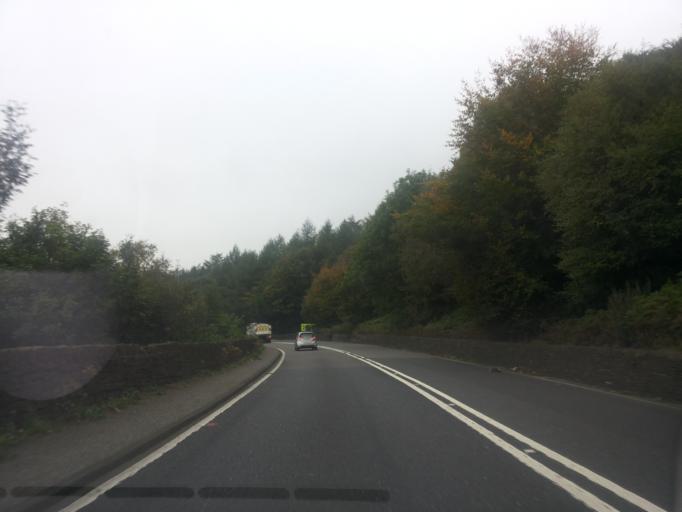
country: GB
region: England
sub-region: Derbyshire
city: Glossop
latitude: 53.4843
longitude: -1.9273
